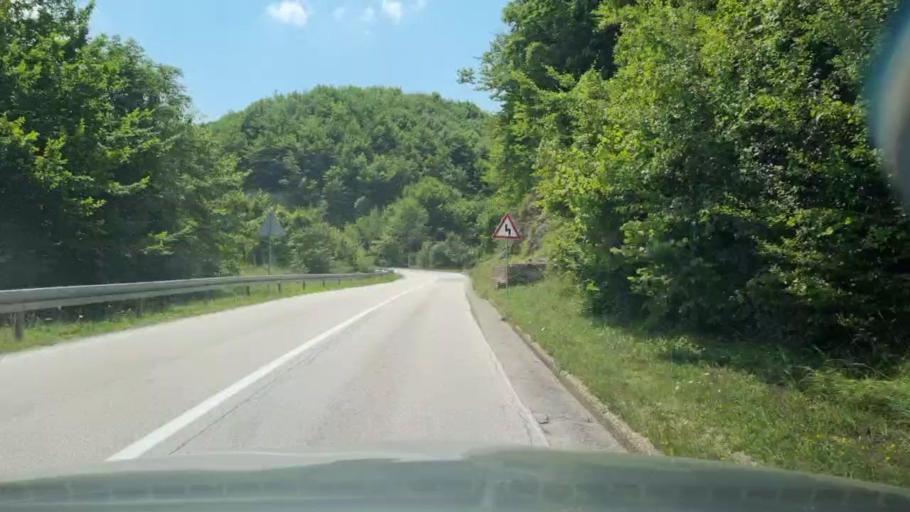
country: BA
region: Federation of Bosnia and Herzegovina
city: Tojsici
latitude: 44.5448
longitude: 18.8630
